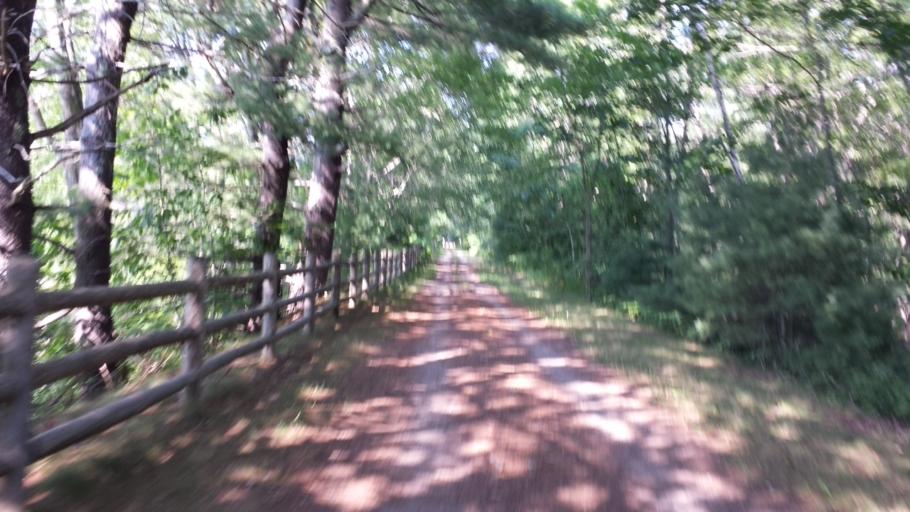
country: US
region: Maine
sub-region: York County
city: Biddeford
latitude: 43.4568
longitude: -70.5075
